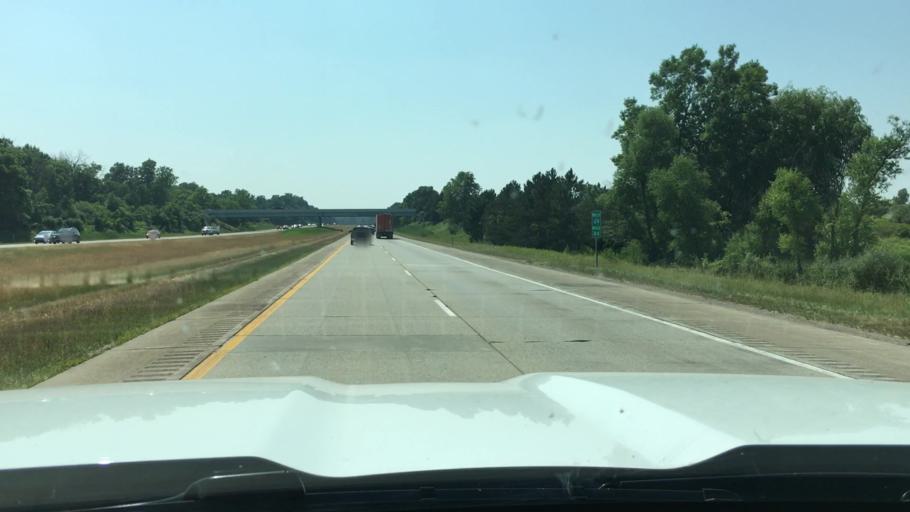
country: US
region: Michigan
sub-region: Clinton County
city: DeWitt
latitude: 42.8078
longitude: -84.5985
